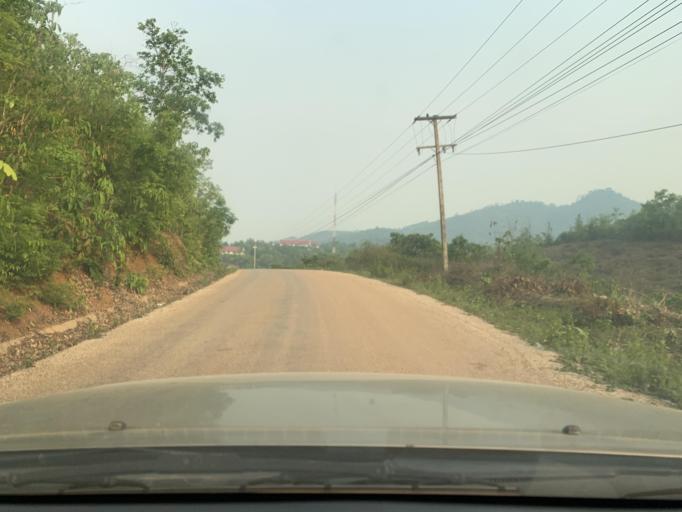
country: LA
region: Louangphabang
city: Louangphabang
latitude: 19.9112
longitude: 102.0798
